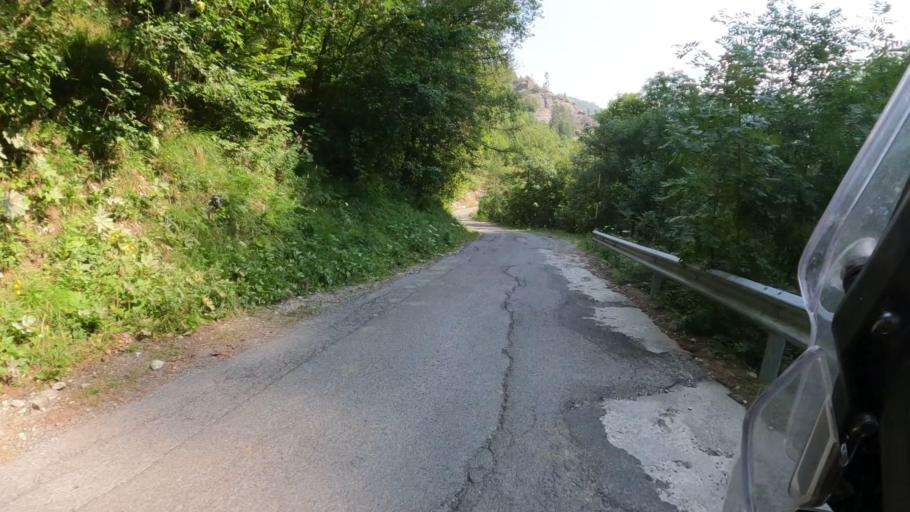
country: IT
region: Piedmont
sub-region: Provincia di Cuneo
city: Canosio
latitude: 44.4496
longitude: 7.0704
